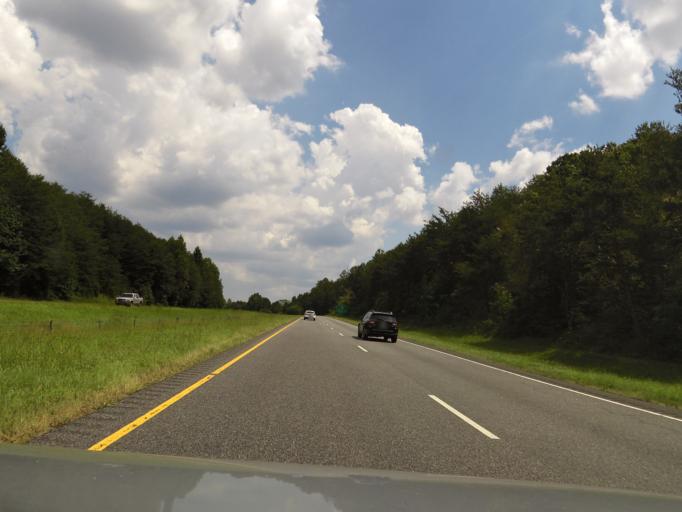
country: US
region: North Carolina
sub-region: Polk County
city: Columbus
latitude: 35.2791
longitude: -82.1254
